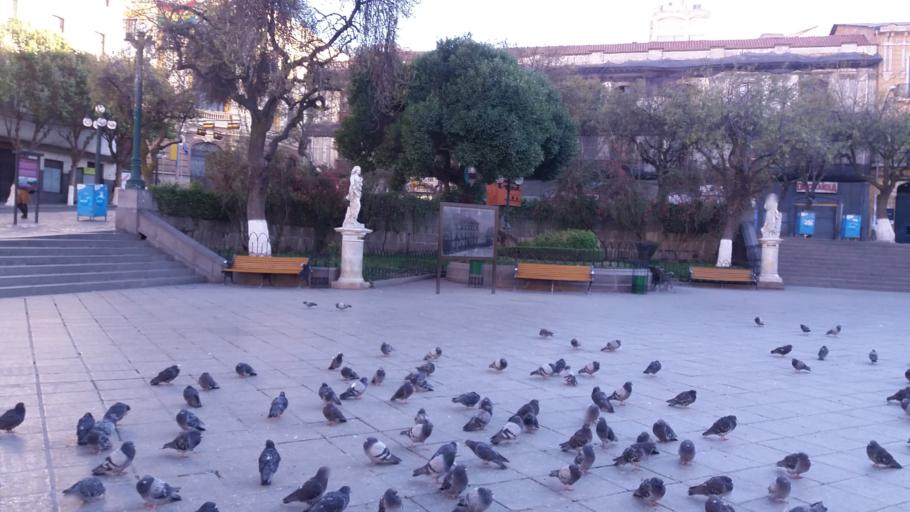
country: BO
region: La Paz
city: La Paz
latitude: -16.4957
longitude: -68.1337
